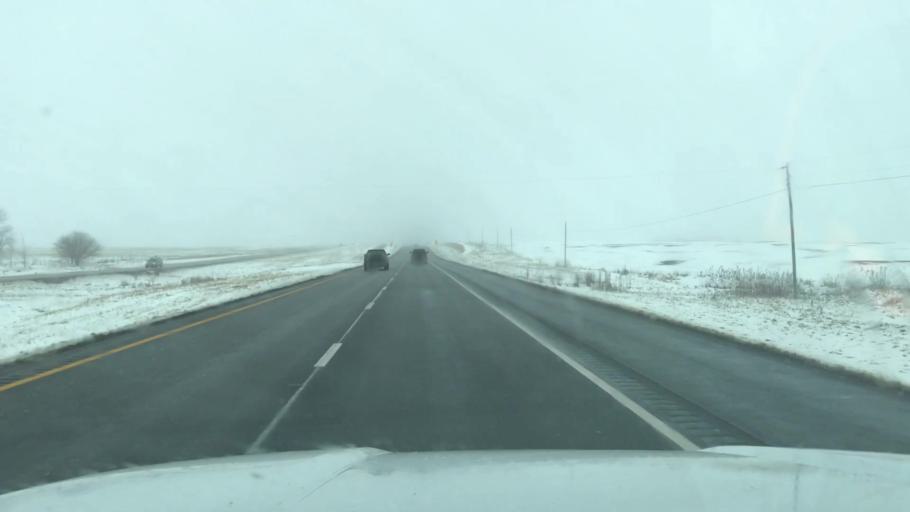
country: US
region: Missouri
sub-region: DeKalb County
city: Maysville
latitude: 39.7615
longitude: -94.3728
